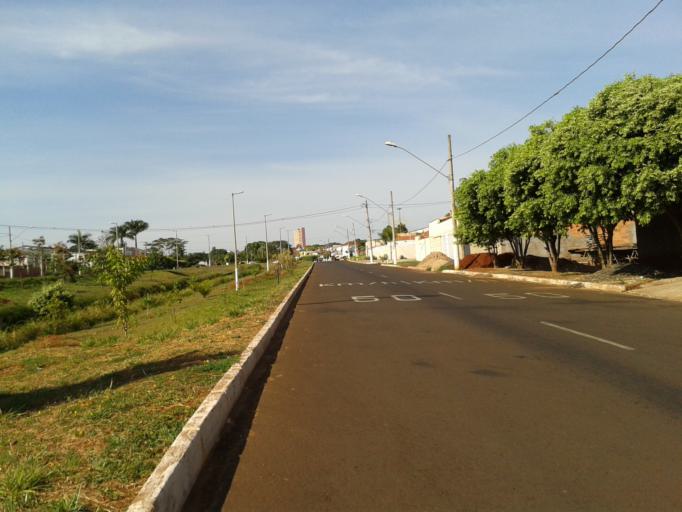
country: BR
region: Minas Gerais
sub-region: Ituiutaba
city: Ituiutaba
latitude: -18.9647
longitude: -49.4610
